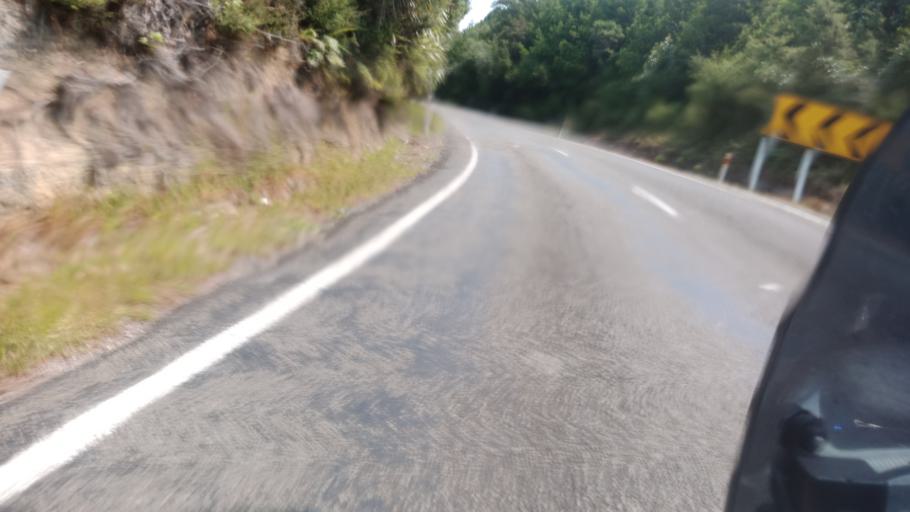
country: NZ
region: Bay of Plenty
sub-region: Opotiki District
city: Opotiki
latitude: -37.5758
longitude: 178.1123
